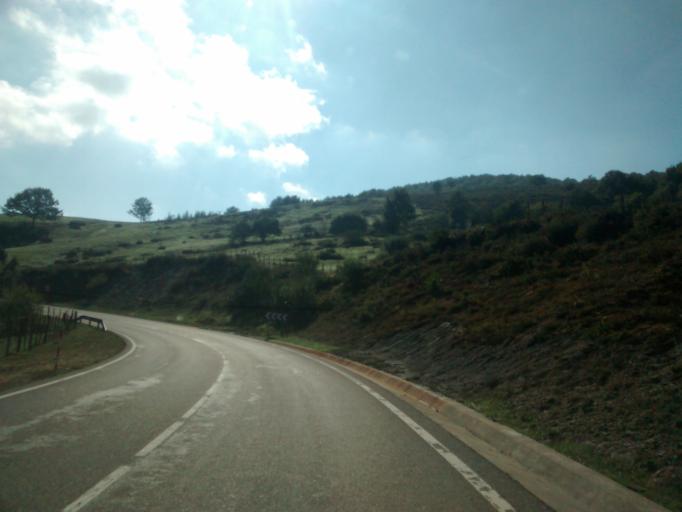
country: ES
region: Cantabria
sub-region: Provincia de Cantabria
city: Reinosa
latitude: 42.9719
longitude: -4.0826
